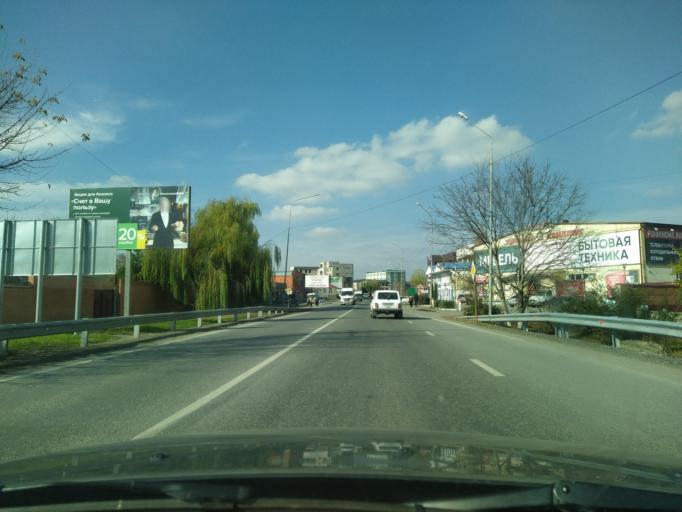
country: RU
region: Ingushetiya
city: Magas
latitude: 43.1969
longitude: 44.7584
